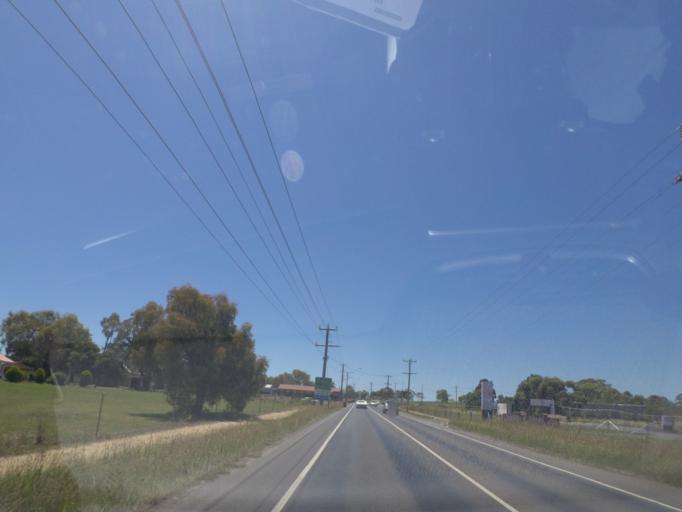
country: AU
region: Victoria
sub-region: Whittlesea
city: Epping
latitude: -37.5959
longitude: 145.0334
